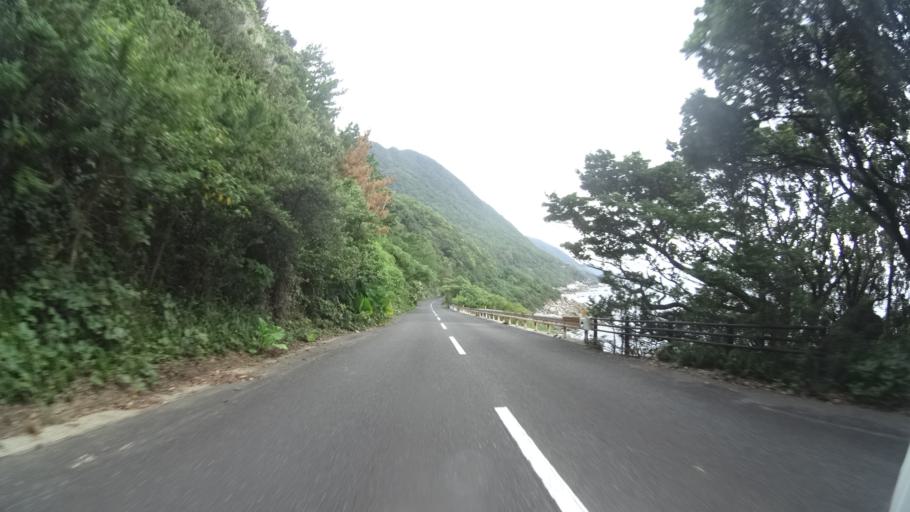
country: JP
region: Kagoshima
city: Nishinoomote
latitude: 30.3167
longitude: 130.4033
